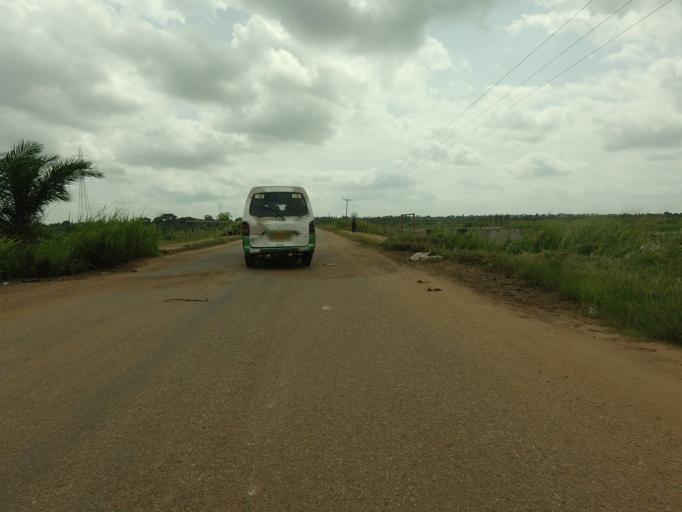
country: TG
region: Maritime
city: Lome
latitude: 6.1694
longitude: 1.0831
